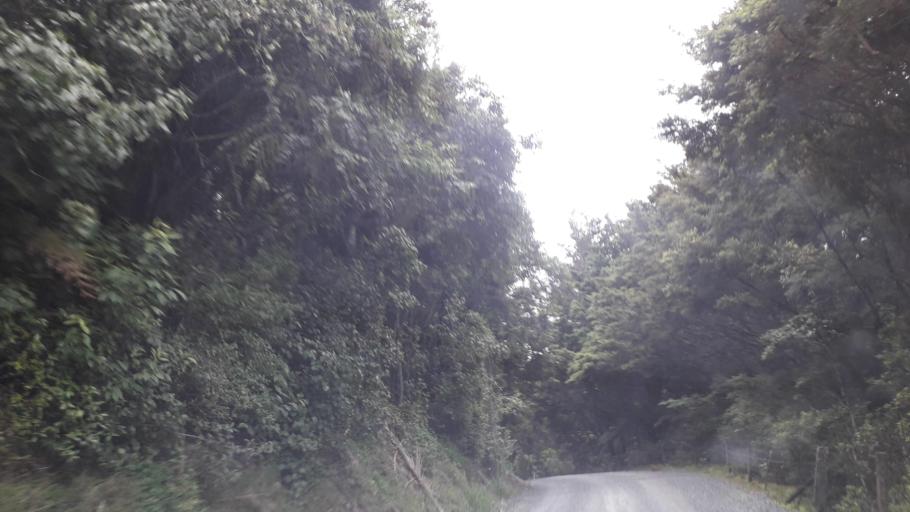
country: NZ
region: Northland
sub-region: Far North District
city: Taipa
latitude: -35.0688
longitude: 173.5531
